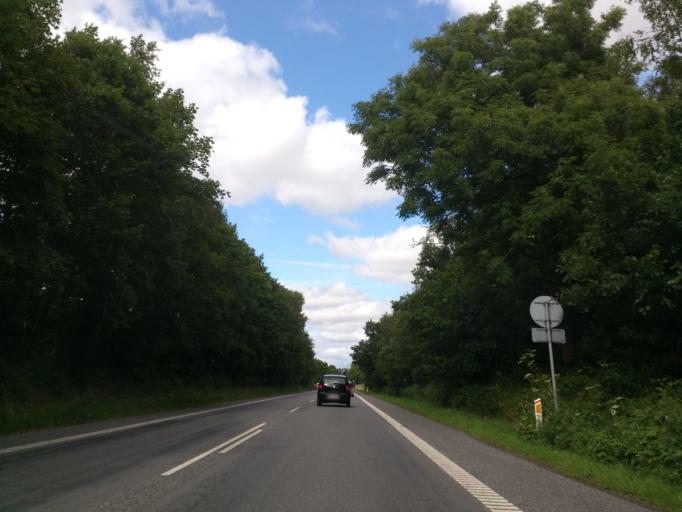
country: DK
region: South Denmark
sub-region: Aabenraa Kommune
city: Krusa
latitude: 54.9013
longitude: 9.4347
